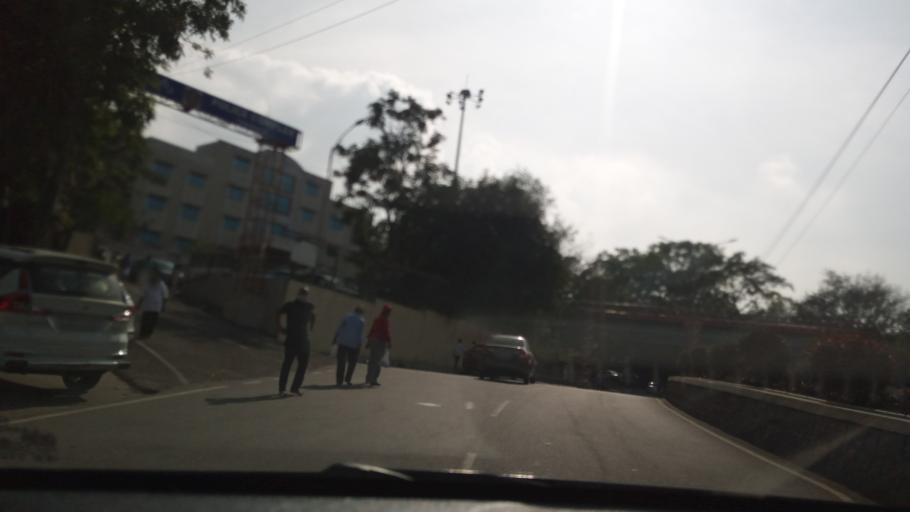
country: IN
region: Andhra Pradesh
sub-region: Chittoor
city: Tirumala
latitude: 13.6835
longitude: 79.3512
